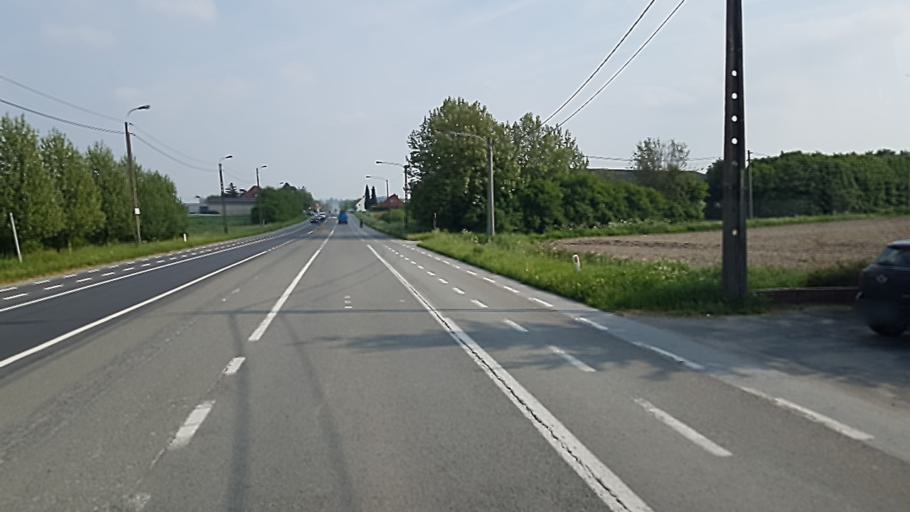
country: BE
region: Flanders
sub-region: Provincie West-Vlaanderen
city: Kortrijk
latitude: 50.7947
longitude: 3.2891
